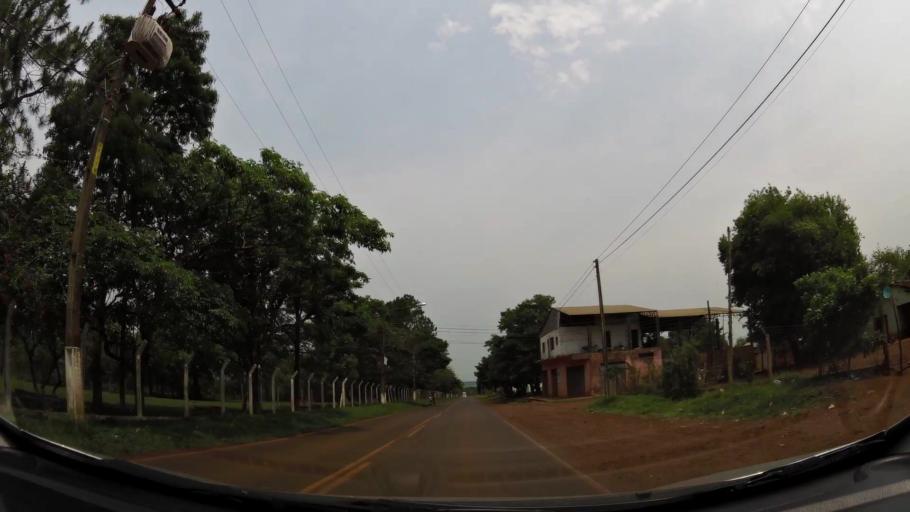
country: BR
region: Parana
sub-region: Foz Do Iguacu
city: Foz do Iguacu
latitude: -25.5773
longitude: -54.6030
